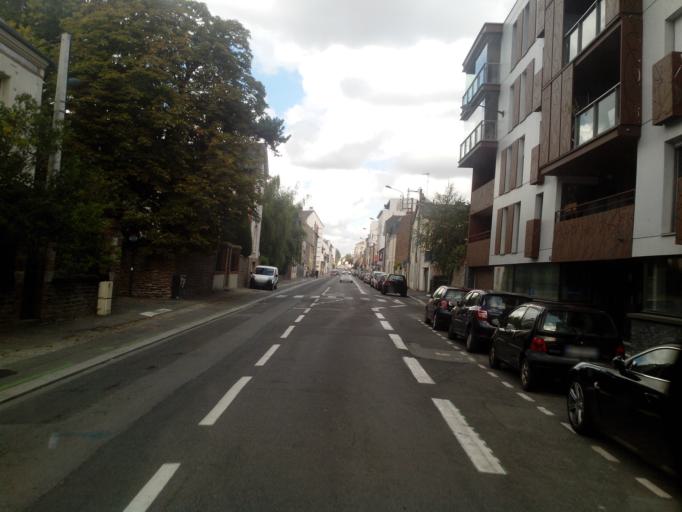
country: FR
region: Brittany
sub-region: Departement d'Ille-et-Vilaine
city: Rennes
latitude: 48.1169
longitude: -1.6588
